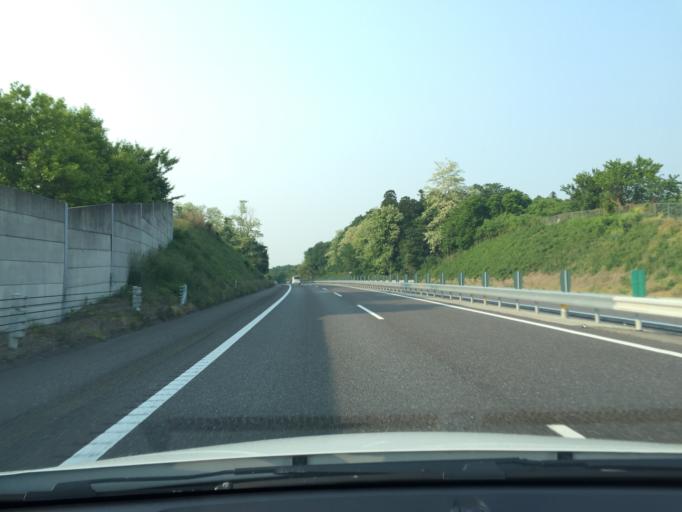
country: JP
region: Fukushima
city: Sukagawa
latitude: 37.2313
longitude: 140.3251
